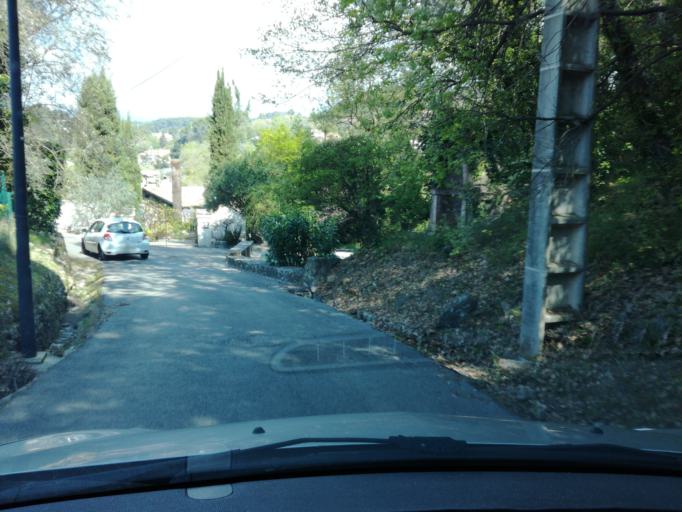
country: FR
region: Provence-Alpes-Cote d'Azur
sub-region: Departement des Alpes-Maritimes
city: Mougins
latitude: 43.6041
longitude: 6.9956
